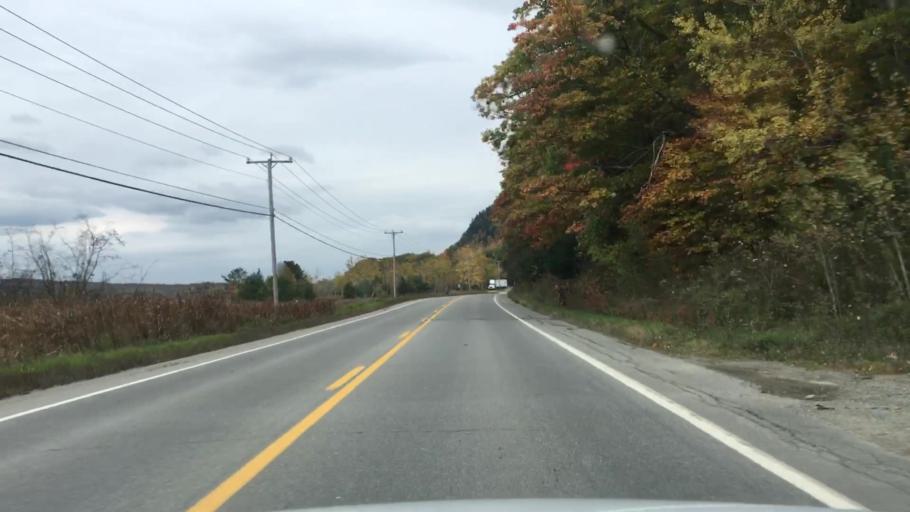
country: US
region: Maine
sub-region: Waldo County
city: Frankfort
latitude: 44.5941
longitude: -68.8655
